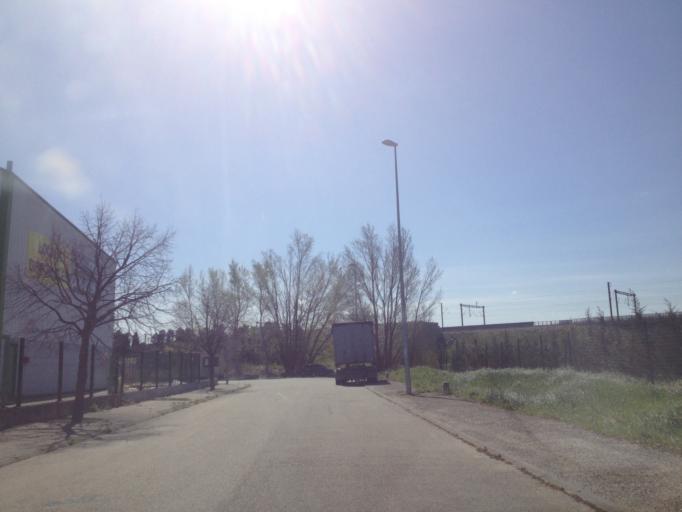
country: FR
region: Languedoc-Roussillon
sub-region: Departement du Gard
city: Les Angles
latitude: 43.9296
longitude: 4.7708
